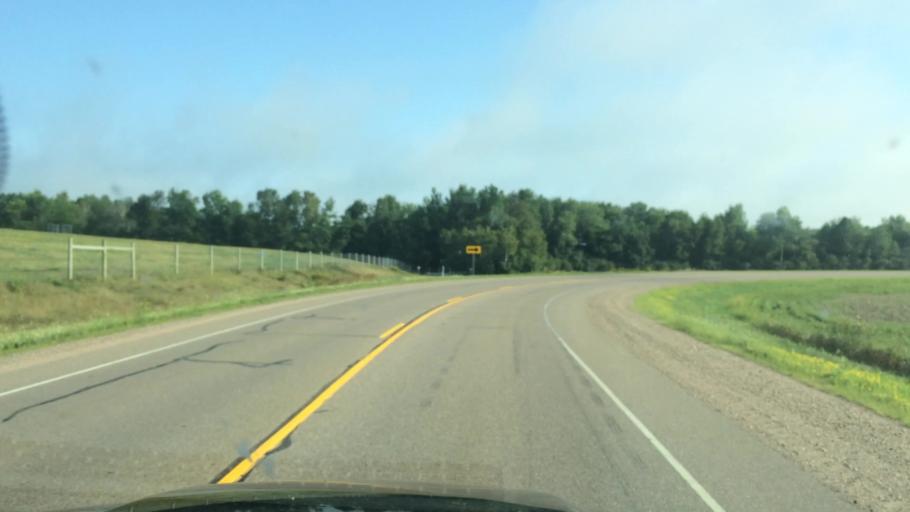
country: US
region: Wisconsin
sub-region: Langlade County
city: Antigo
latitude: 45.1608
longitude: -89.1618
